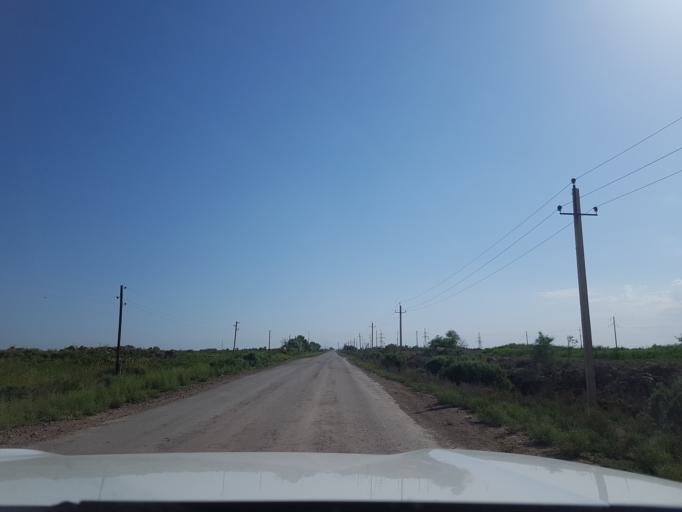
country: TM
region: Dasoguz
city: Koeneuergench
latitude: 42.0950
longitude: 58.8945
